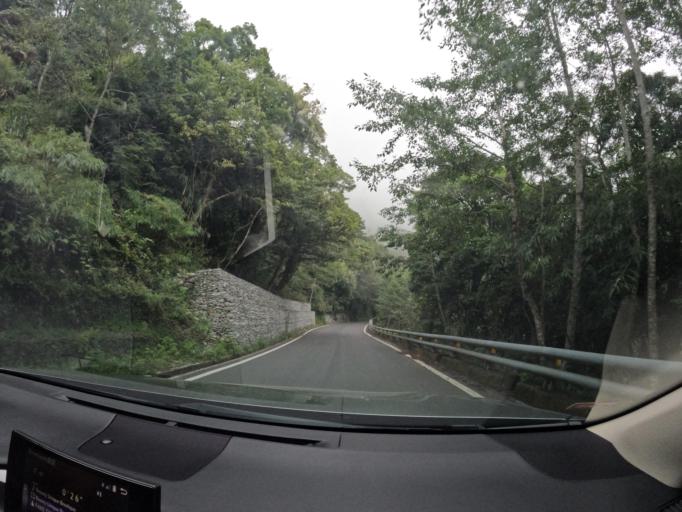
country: TW
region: Taiwan
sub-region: Taitung
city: Taitung
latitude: 23.2393
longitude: 120.9842
